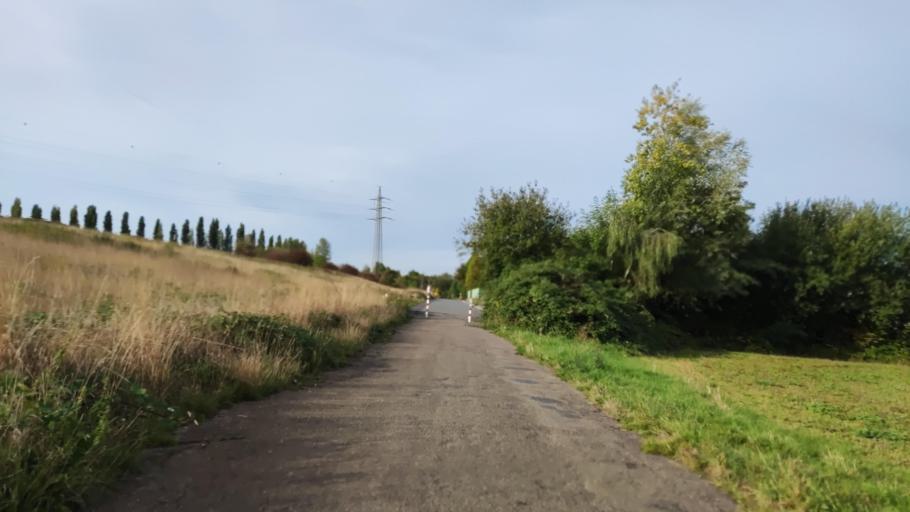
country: DE
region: North Rhine-Westphalia
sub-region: Regierungsbezirk Arnsberg
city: Herne
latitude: 51.5454
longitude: 7.2561
